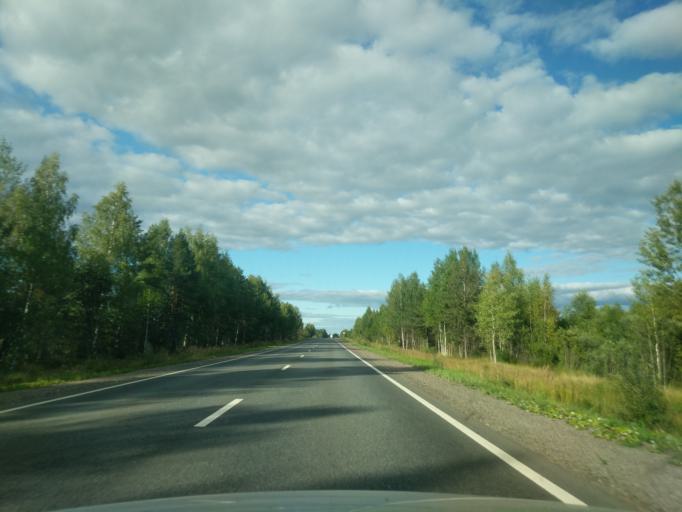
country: RU
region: Kostroma
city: Manturovo
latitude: 58.2301
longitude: 44.6314
